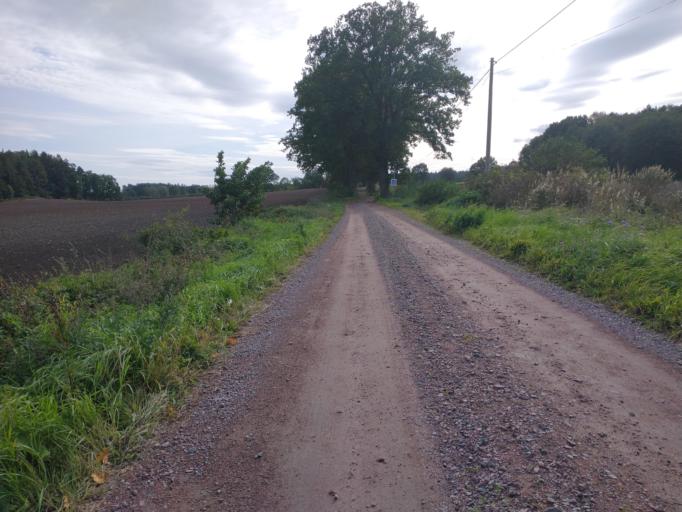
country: SE
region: Kalmar
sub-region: Kalmar Kommun
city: Lindsdal
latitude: 56.7761
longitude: 16.3080
